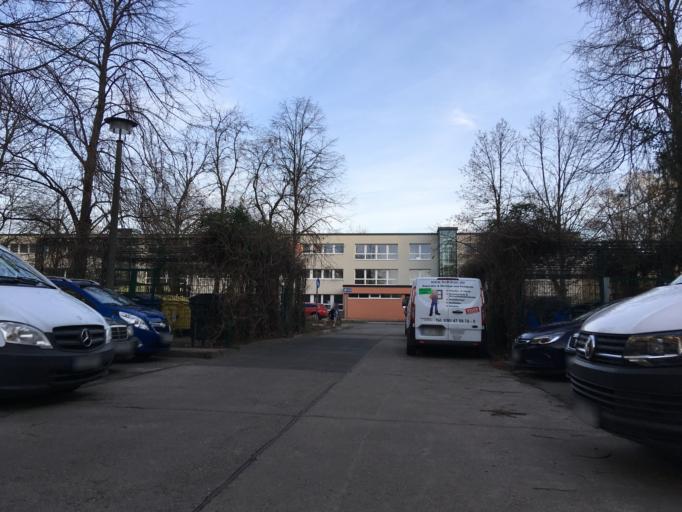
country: DE
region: Berlin
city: Buch
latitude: 52.6268
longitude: 13.4928
